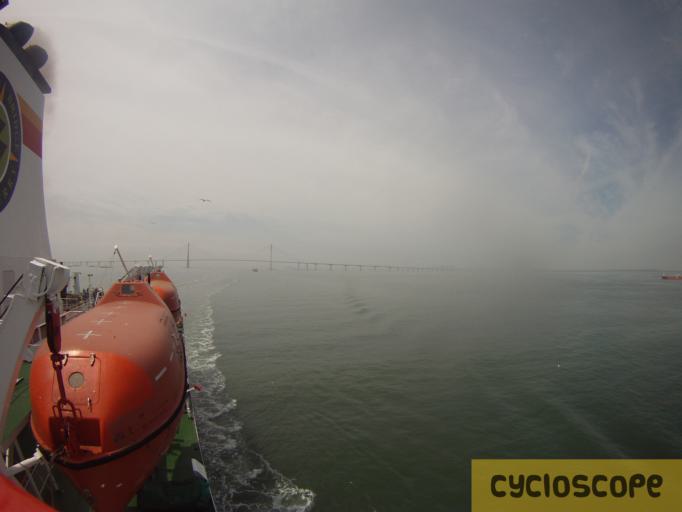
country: KR
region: Incheon
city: Incheon
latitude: 37.4514
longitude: 126.5827
